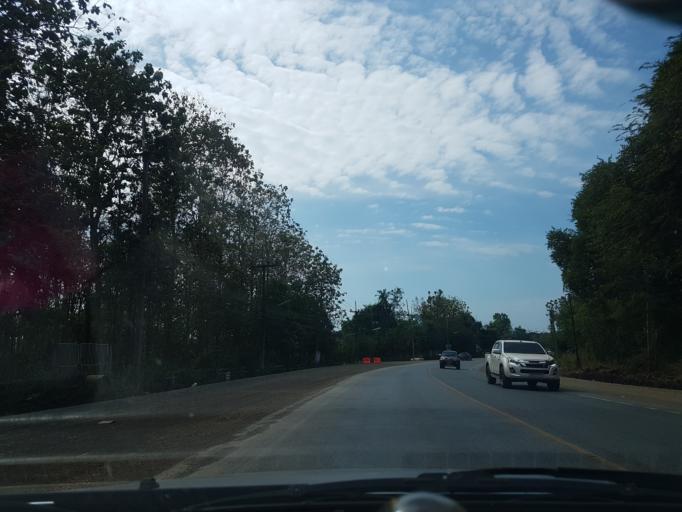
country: TH
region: Sara Buri
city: Phra Phutthabat
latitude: 14.8030
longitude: 100.7578
